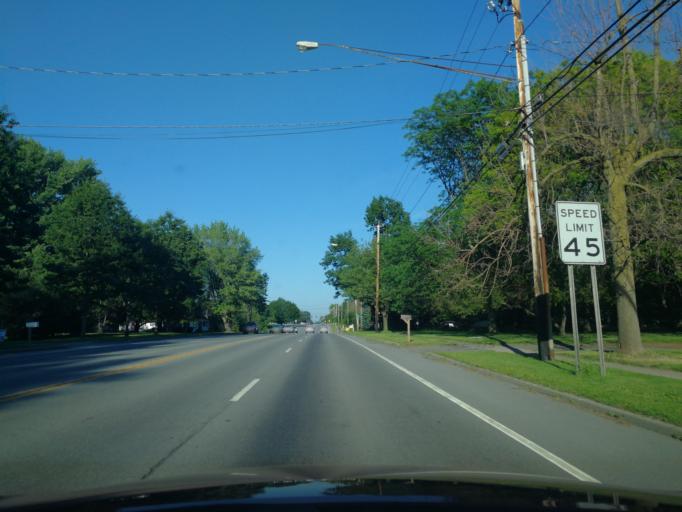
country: US
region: New York
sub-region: Monroe County
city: Greece
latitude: 43.2531
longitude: -77.7116
